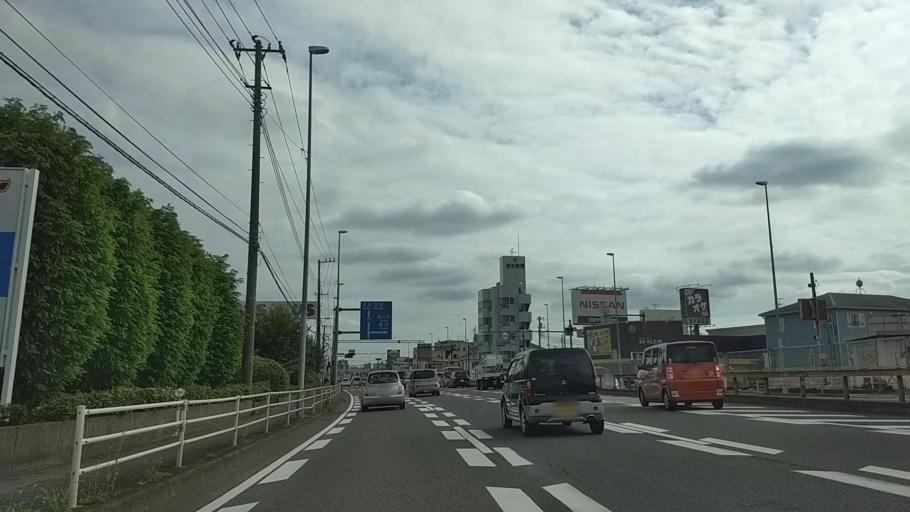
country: JP
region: Kanagawa
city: Atsugi
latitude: 35.4618
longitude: 139.3598
